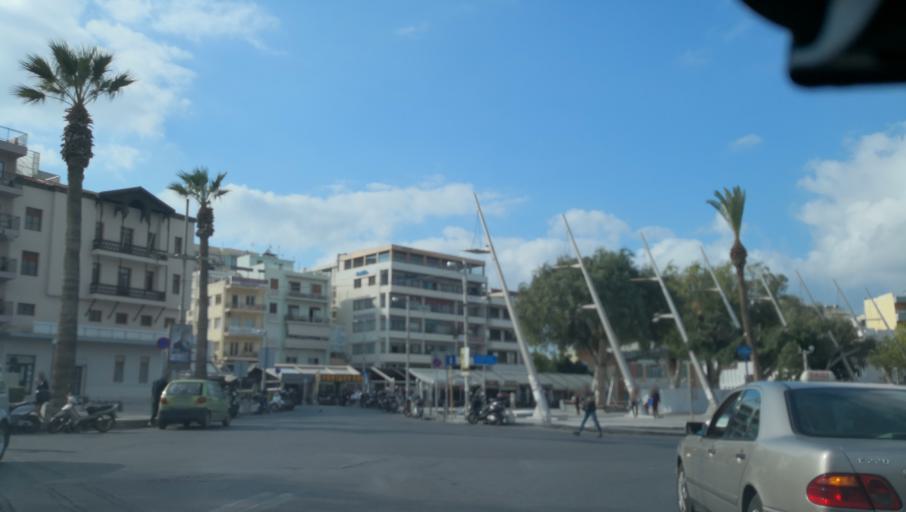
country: GR
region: Crete
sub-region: Nomos Irakleiou
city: Irakleion
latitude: 35.3371
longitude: 25.1370
